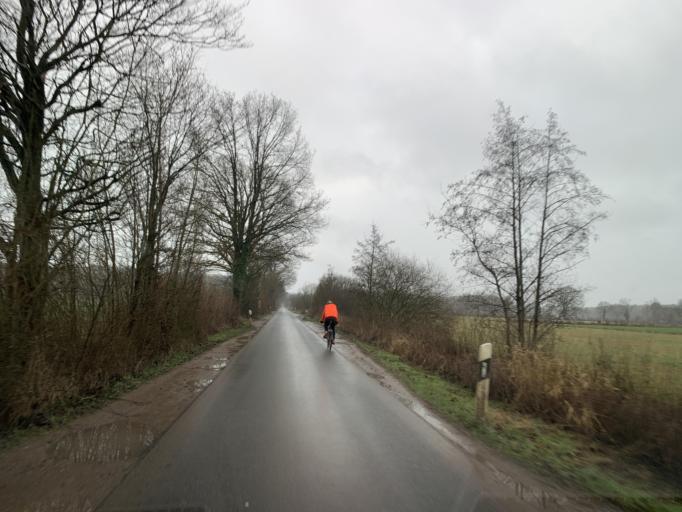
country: DE
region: North Rhine-Westphalia
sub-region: Regierungsbezirk Munster
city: Senden
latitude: 51.8964
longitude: 7.5239
